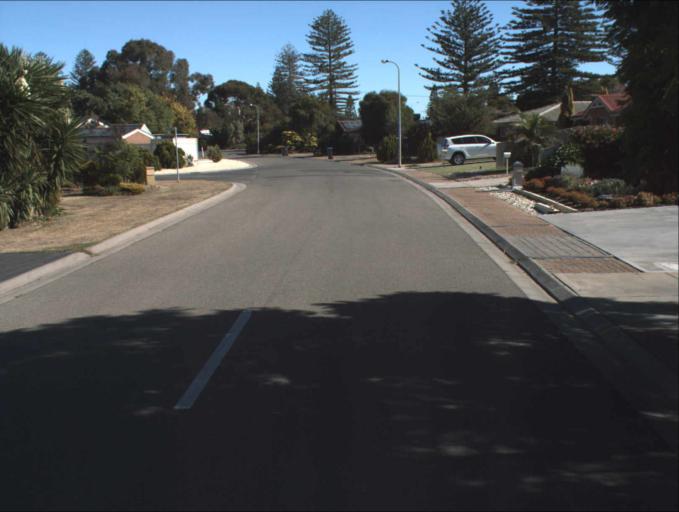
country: AU
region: South Australia
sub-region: Port Adelaide Enfield
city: Birkenhead
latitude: -34.7820
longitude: 138.4901
